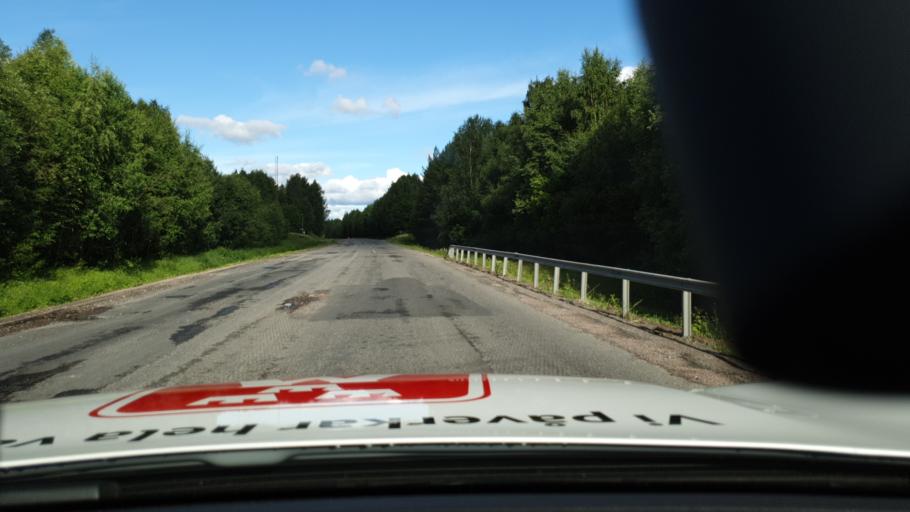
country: SE
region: Norrbotten
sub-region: Bodens Kommun
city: Boden
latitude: 65.8463
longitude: 21.5958
